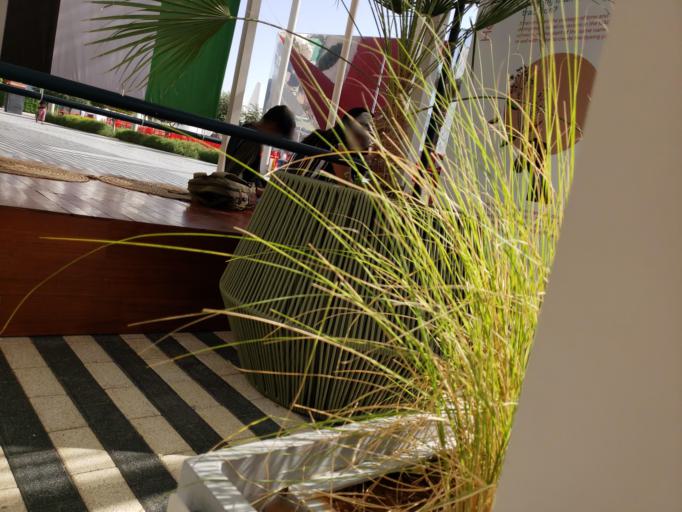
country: AE
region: Dubai
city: Dubai
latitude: 24.9639
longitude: 55.1528
